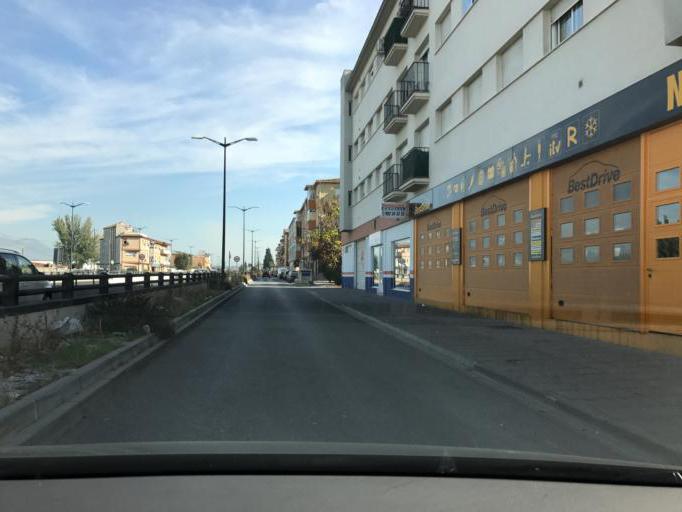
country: ES
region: Andalusia
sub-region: Provincia de Granada
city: Atarfe
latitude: 37.1923
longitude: -3.7133
